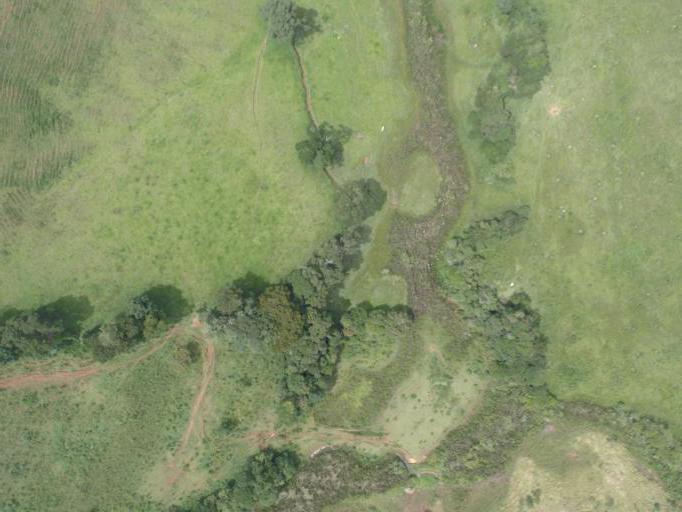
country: BR
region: Minas Gerais
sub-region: Tiradentes
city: Tiradentes
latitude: -21.0692
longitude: -44.0864
